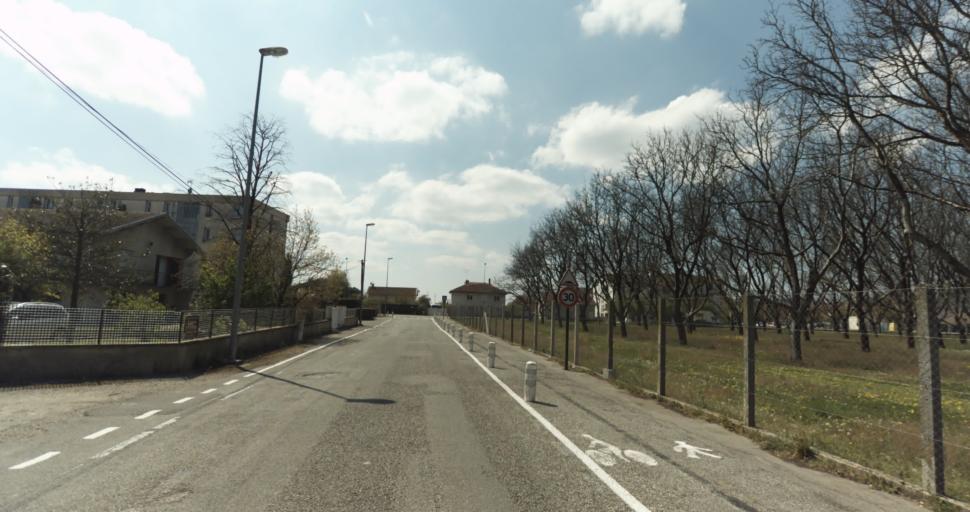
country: FR
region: Rhone-Alpes
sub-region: Departement de l'Isere
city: Saint-Marcellin
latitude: 45.1437
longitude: 5.3192
